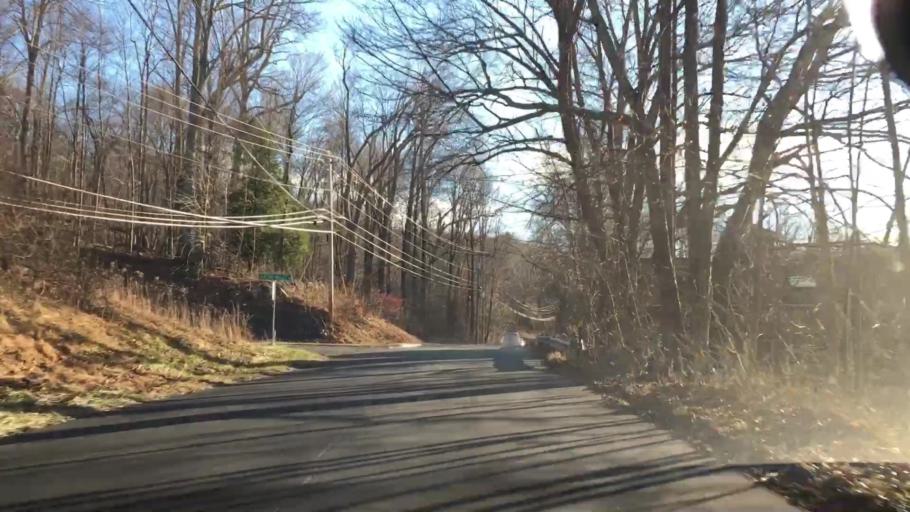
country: US
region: Connecticut
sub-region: Fairfield County
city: Newtown
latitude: 41.4384
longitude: -73.3146
